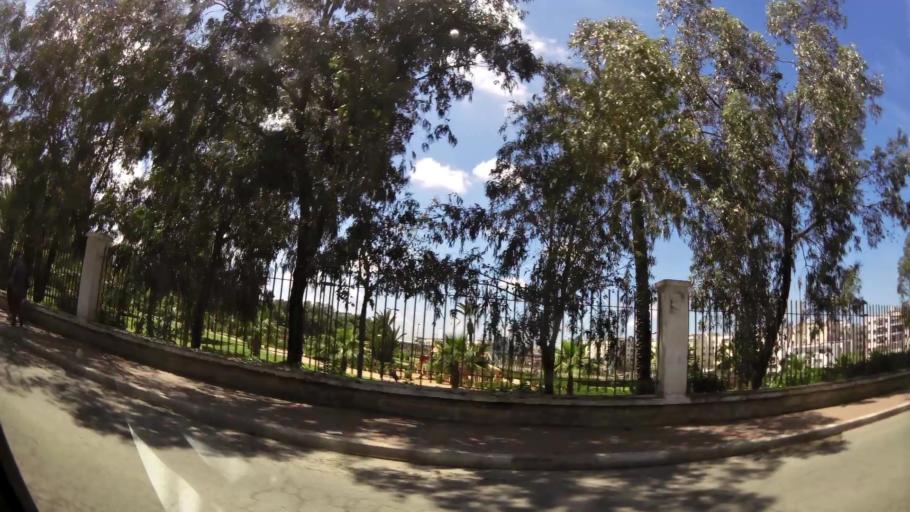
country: MA
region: Grand Casablanca
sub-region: Casablanca
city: Casablanca
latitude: 33.5649
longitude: -7.5780
